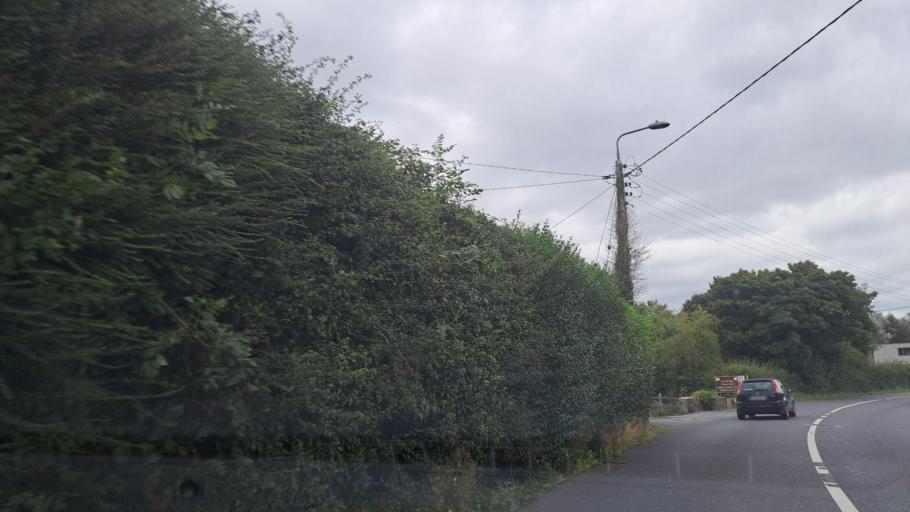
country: IE
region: Ulster
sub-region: An Cabhan
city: Bailieborough
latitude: 53.9921
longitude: -6.9005
